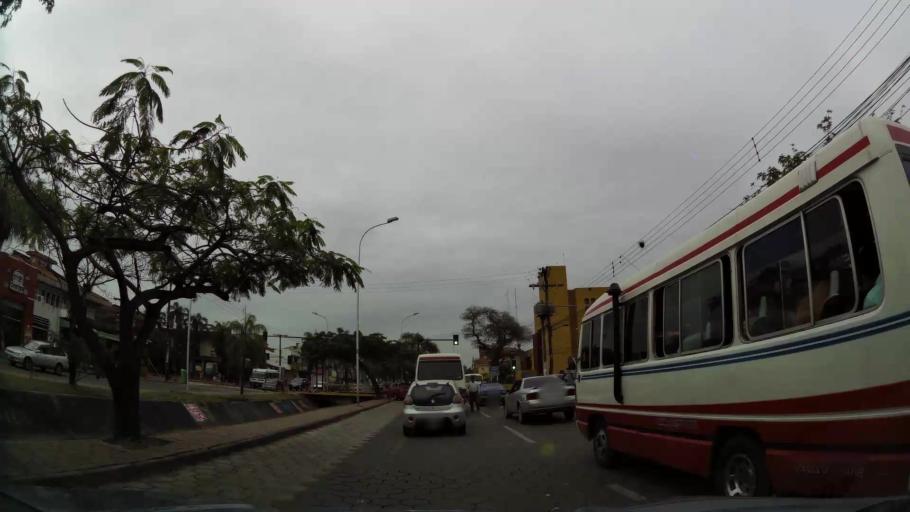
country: BO
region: Santa Cruz
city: Santa Cruz de la Sierra
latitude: -17.7912
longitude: -63.1969
